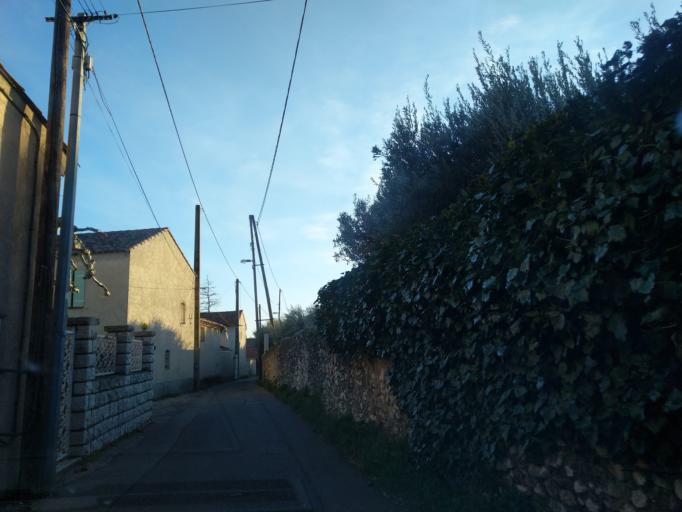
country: FR
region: Provence-Alpes-Cote d'Azur
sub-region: Departement des Bouches-du-Rhone
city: Plan-de-Cuques
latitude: 43.3413
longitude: 5.4510
